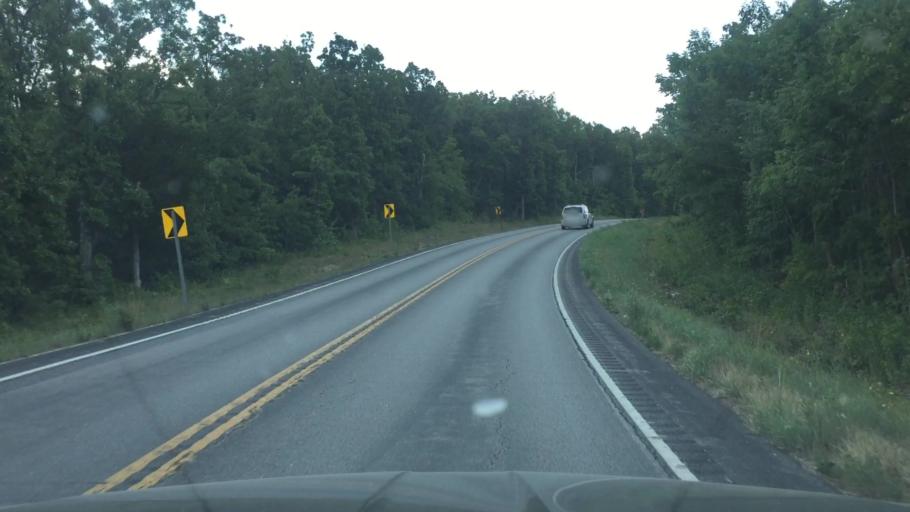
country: US
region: Missouri
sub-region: Miller County
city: Tuscumbia
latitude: 38.0989
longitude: -92.4962
